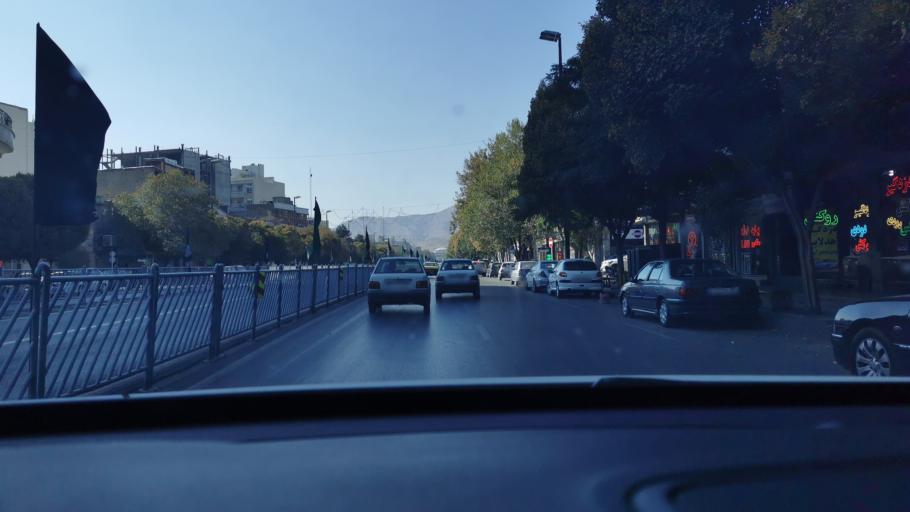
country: IR
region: Razavi Khorasan
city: Mashhad
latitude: 36.2728
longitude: 59.6026
